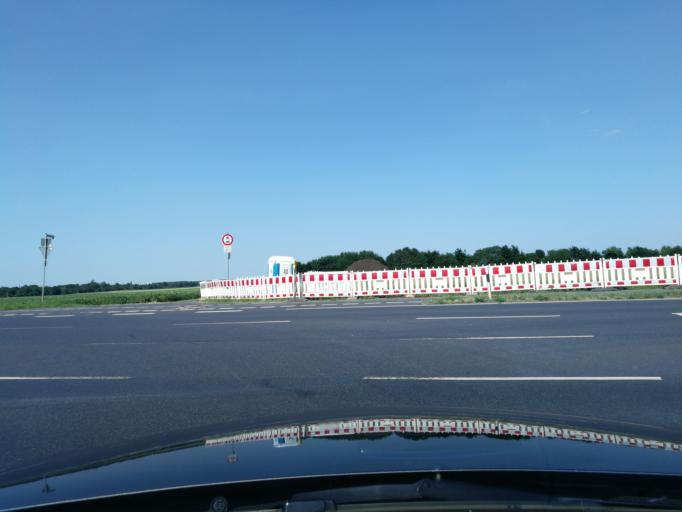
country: DE
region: North Rhine-Westphalia
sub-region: Regierungsbezirk Dusseldorf
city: Grevenbroich
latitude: 51.0910
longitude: 6.6191
